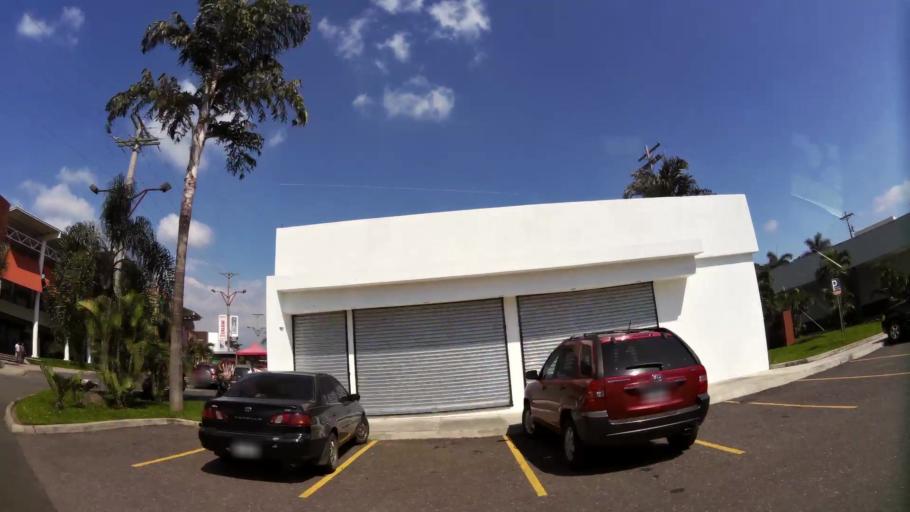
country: GT
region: Suchitepeque
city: Mazatenango
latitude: 14.5349
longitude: -91.4950
